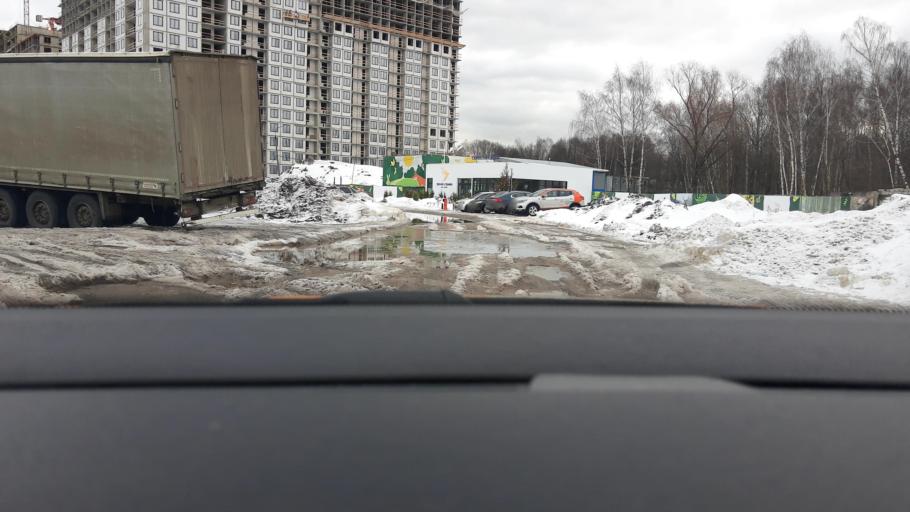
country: RU
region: Moscow
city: Babushkin
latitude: 55.8477
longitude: 37.7110
